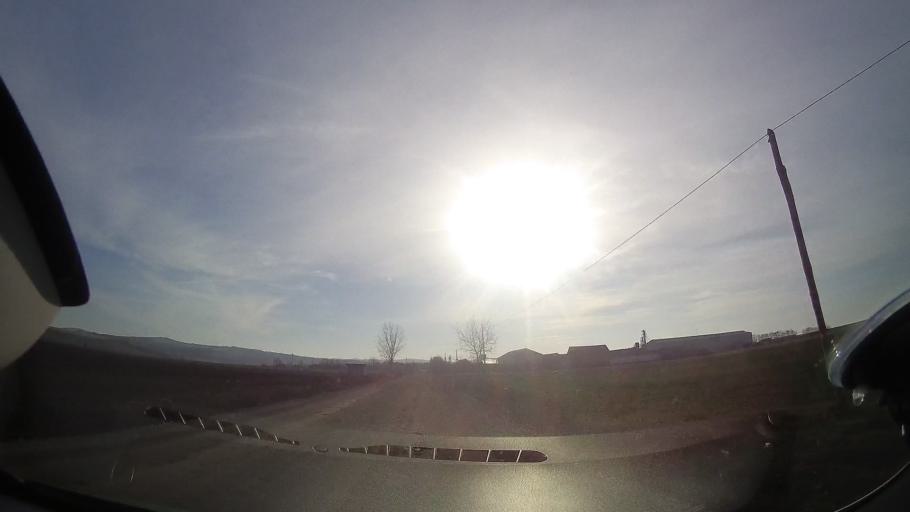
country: RO
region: Bihor
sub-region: Comuna Sarbi
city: Sarbi
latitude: 47.2139
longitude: 22.1329
